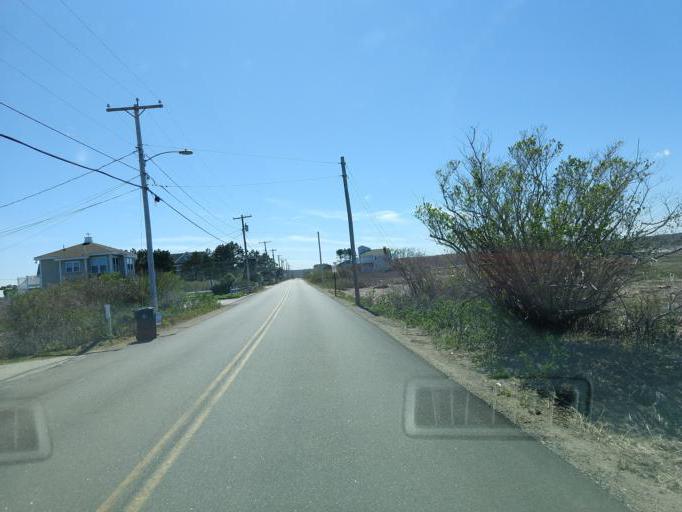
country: US
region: Maine
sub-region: York County
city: Old Orchard Beach
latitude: 43.4408
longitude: -70.3588
